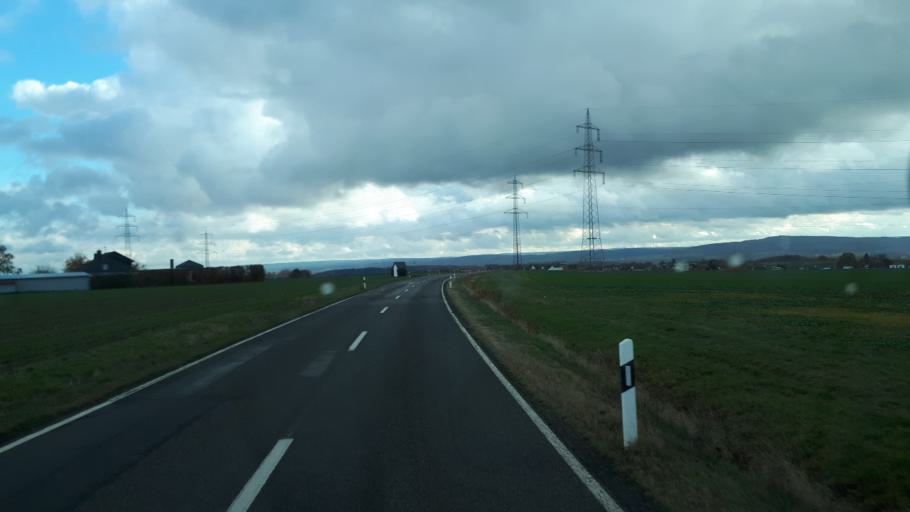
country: DE
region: Rheinland-Pfalz
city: Dunfus
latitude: 50.2137
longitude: 7.2372
